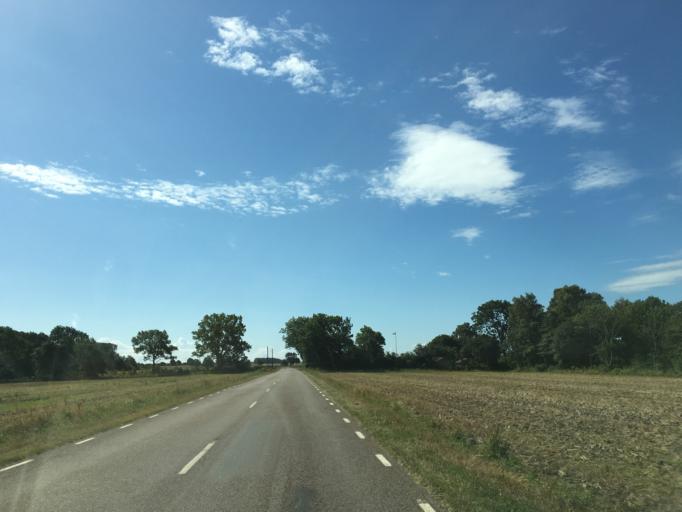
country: SE
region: Kalmar
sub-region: Morbylanga Kommun
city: Moerbylanga
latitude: 56.4074
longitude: 16.4150
